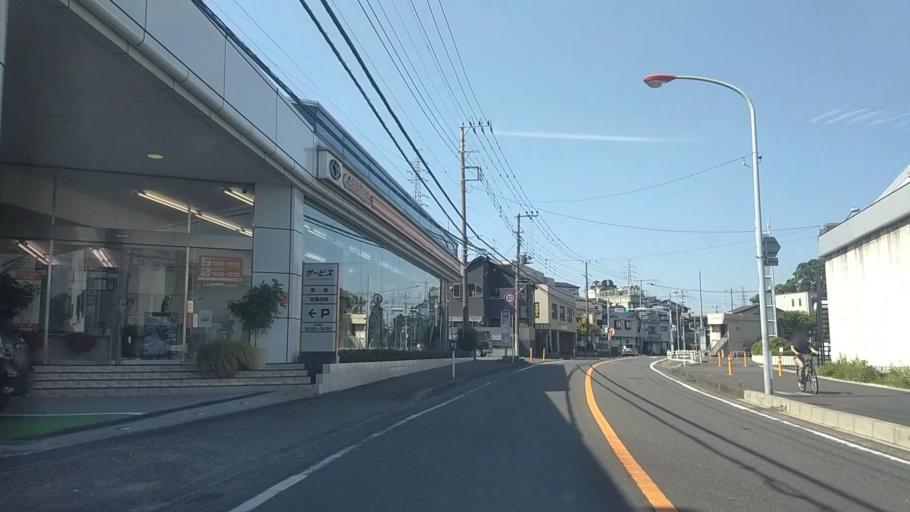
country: JP
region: Kanagawa
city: Kamakura
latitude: 35.3511
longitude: 139.5423
